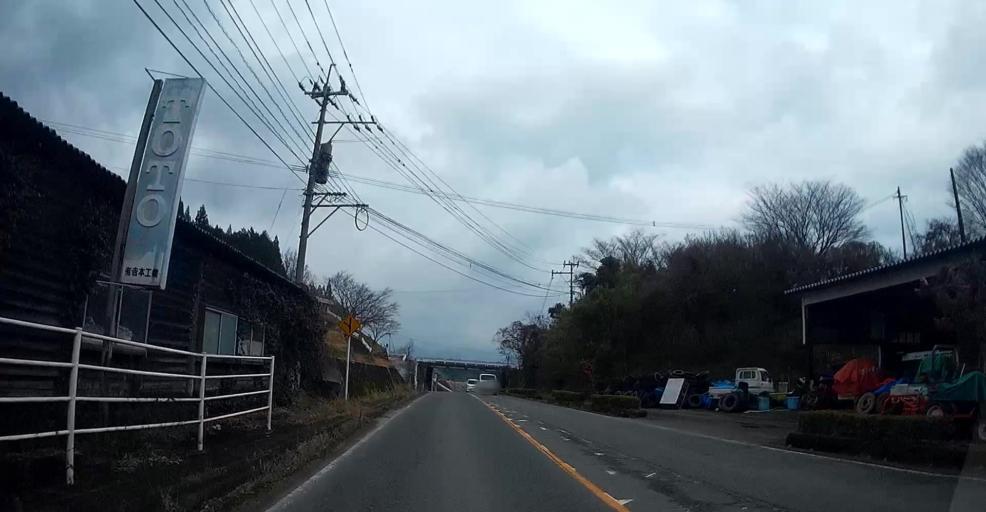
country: JP
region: Kumamoto
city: Matsubase
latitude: 32.6231
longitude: 130.8745
